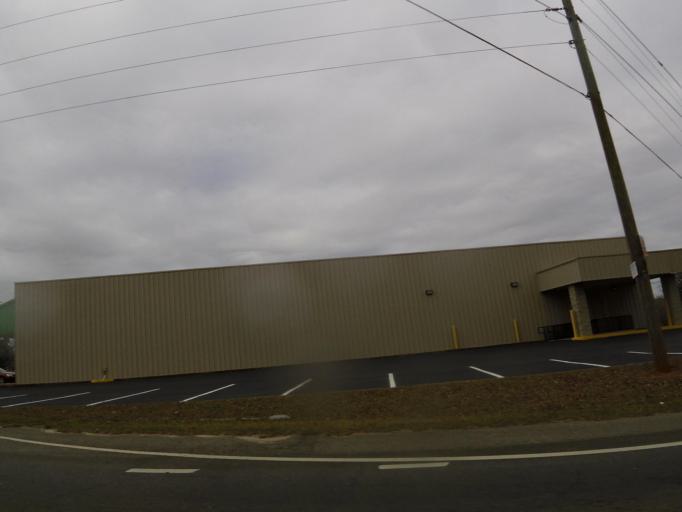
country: US
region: Georgia
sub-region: Randolph County
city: Cuthbert
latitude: 31.7710
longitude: -84.7845
